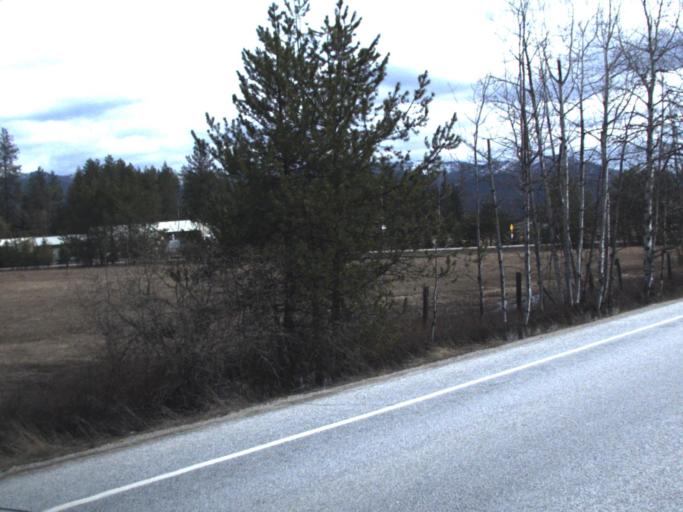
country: US
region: Washington
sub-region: Pend Oreille County
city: Newport
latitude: 48.2306
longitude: -117.1619
